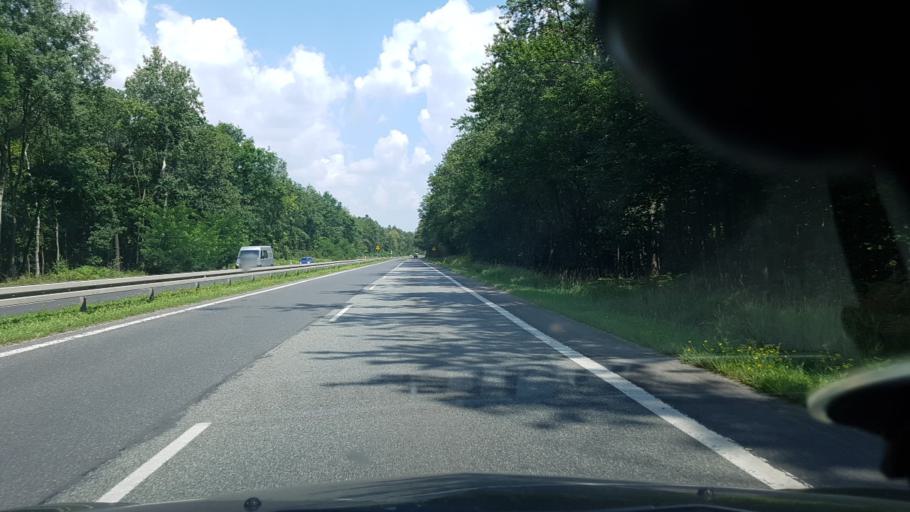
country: PL
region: Silesian Voivodeship
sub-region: Powiat mikolowski
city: Mikolow
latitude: 50.2018
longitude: 18.9444
